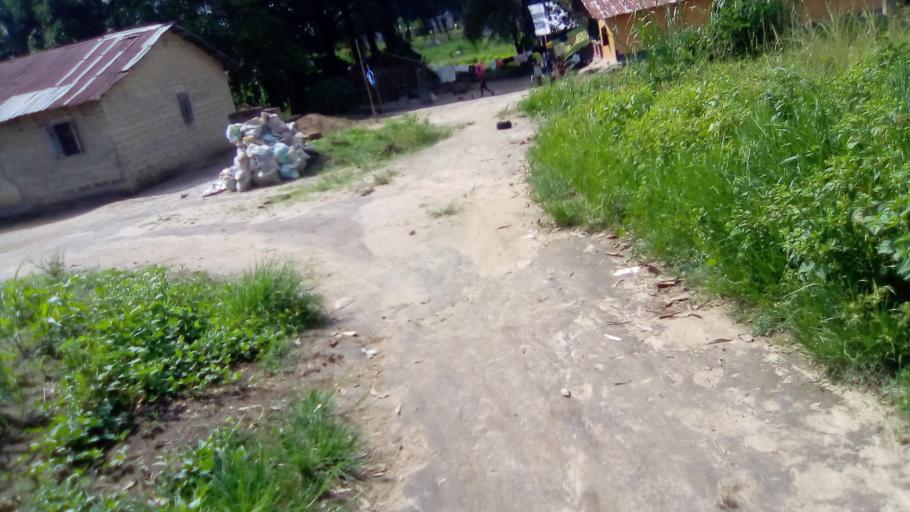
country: SL
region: Southern Province
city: Bo
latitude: 7.9756
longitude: -11.7254
